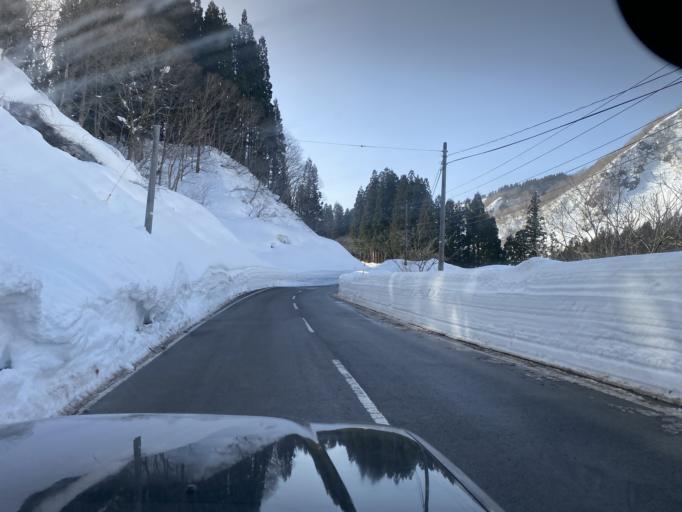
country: JP
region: Toyama
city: Nanto-shi
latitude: 36.4442
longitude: 136.9293
